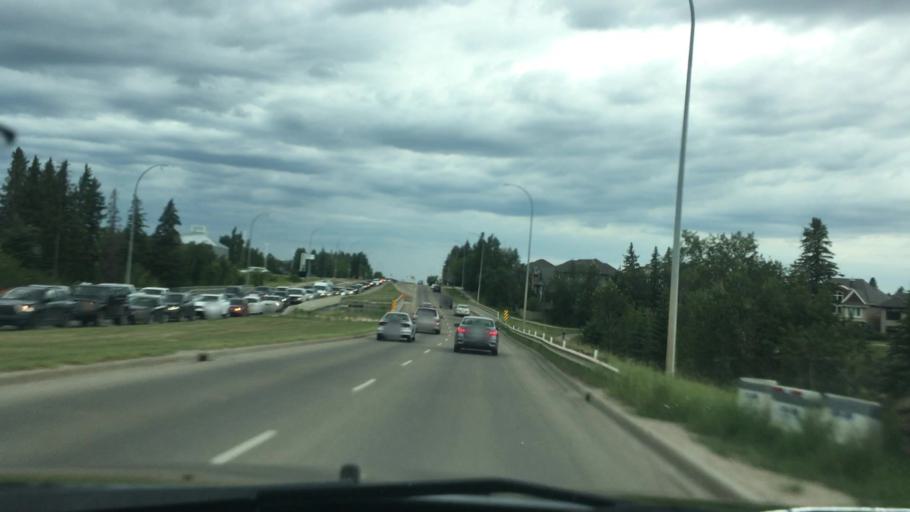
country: CA
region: Alberta
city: Beaumont
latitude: 53.4249
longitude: -113.4971
